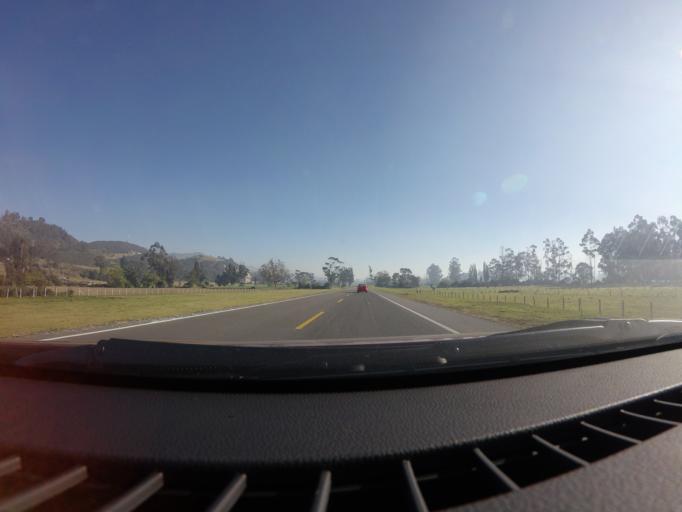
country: CO
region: Cundinamarca
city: Cogua
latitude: 5.0475
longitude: -73.9633
